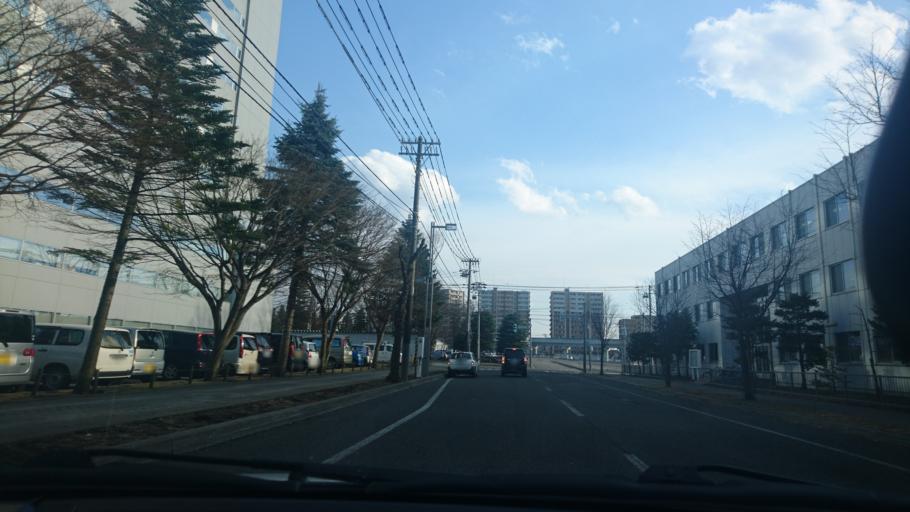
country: JP
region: Hokkaido
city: Obihiro
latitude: 42.9240
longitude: 143.1956
